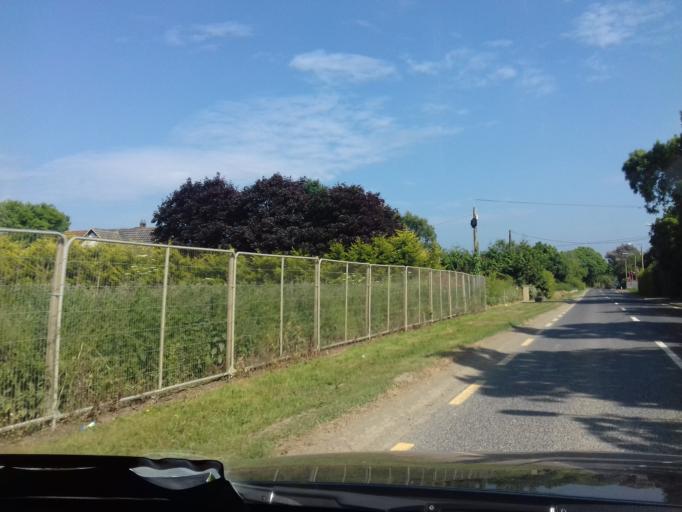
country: IE
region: Leinster
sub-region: Fingal County
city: Swords
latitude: 53.4715
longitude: -6.2491
